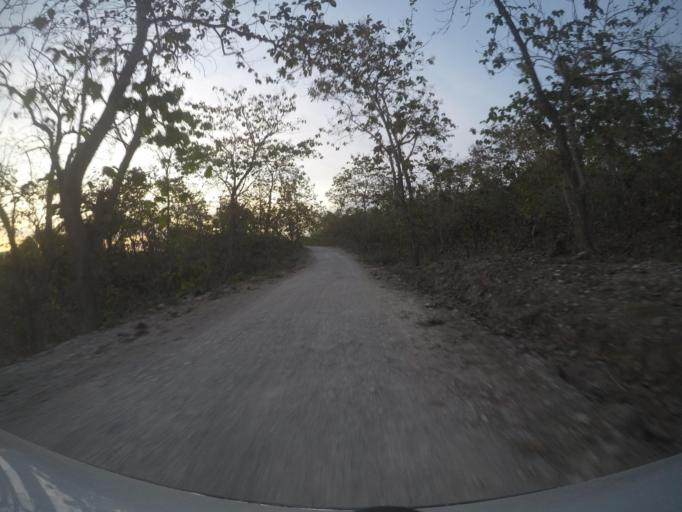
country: TL
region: Viqueque
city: Viqueque
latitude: -8.8946
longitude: 126.3875
